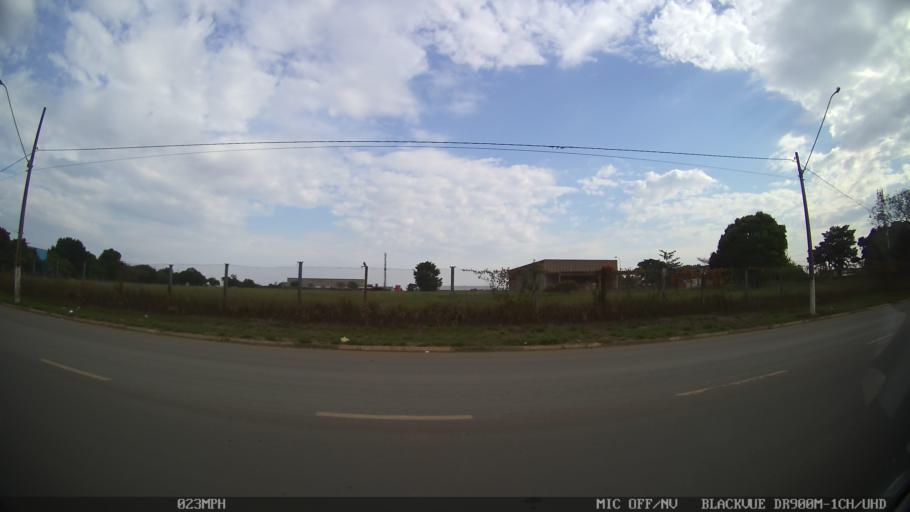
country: BR
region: Sao Paulo
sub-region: Paulinia
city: Paulinia
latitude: -22.7296
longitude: -47.1672
